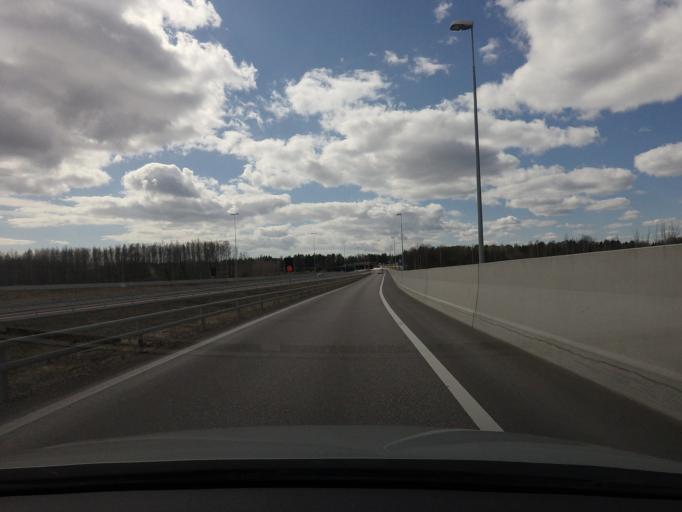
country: FI
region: Kymenlaakso
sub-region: Kotka-Hamina
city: Hamina
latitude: 60.5996
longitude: 27.1863
